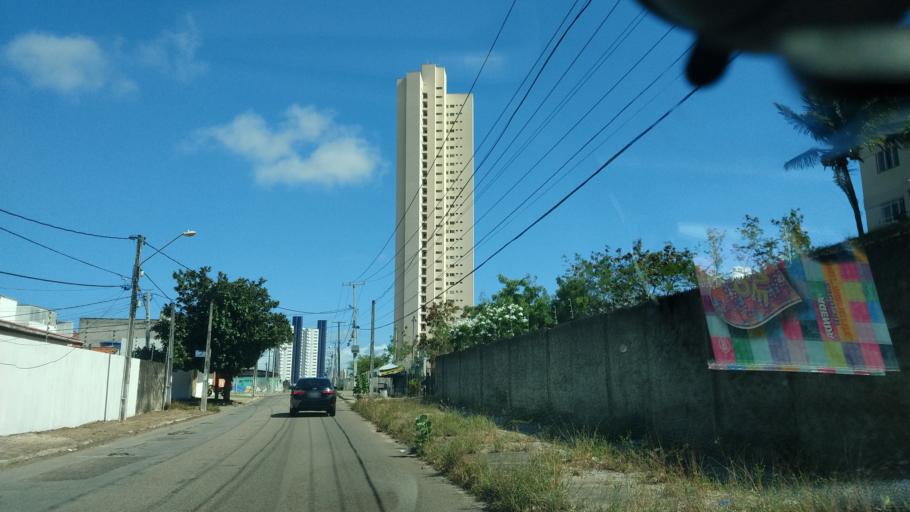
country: BR
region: Rio Grande do Norte
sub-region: Natal
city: Natal
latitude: -5.8685
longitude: -35.1953
